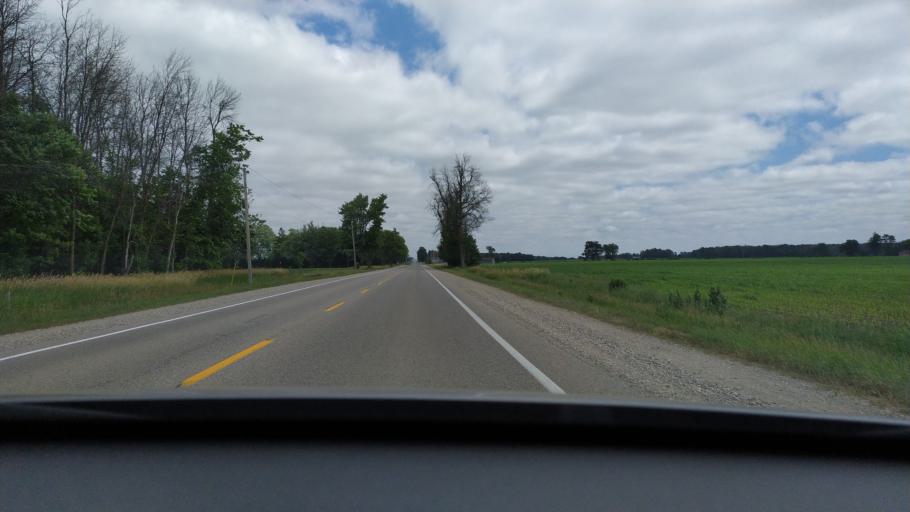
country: CA
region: Ontario
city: Stratford
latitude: 43.3410
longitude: -80.9656
